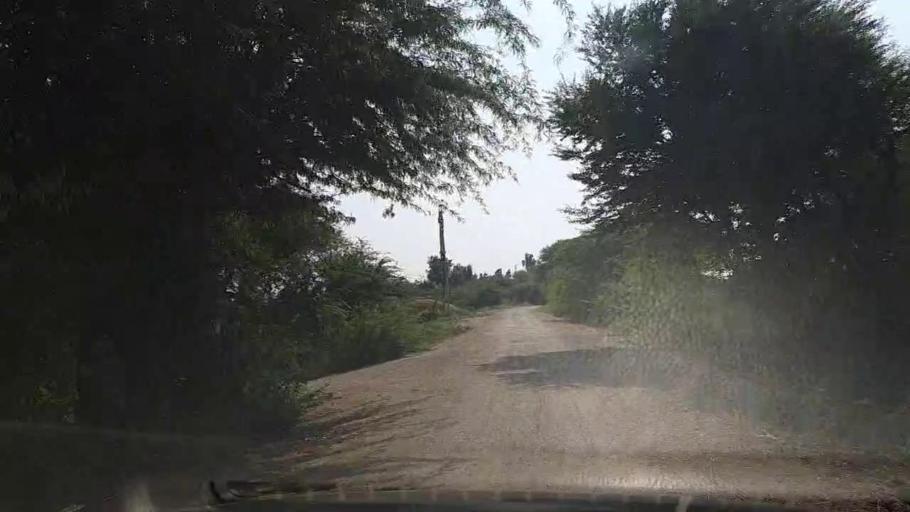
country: PK
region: Sindh
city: Thatta
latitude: 24.7942
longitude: 67.8297
